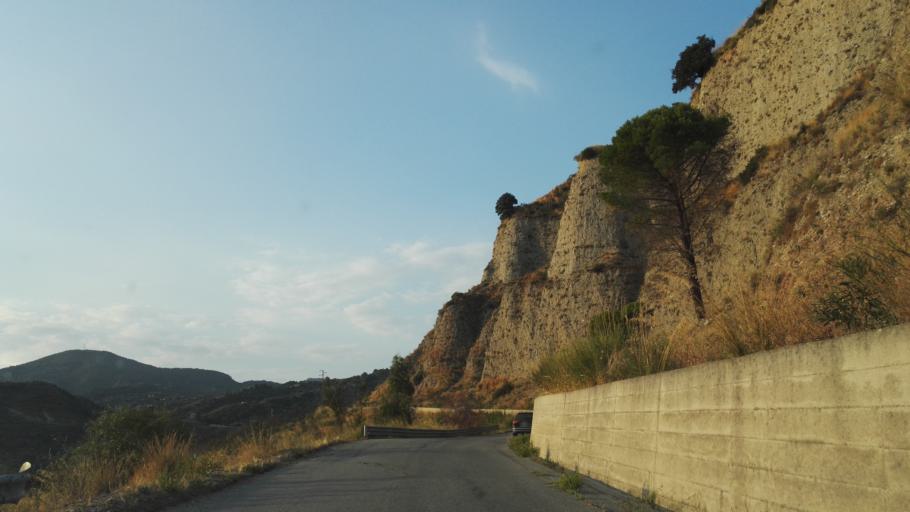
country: IT
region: Calabria
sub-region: Provincia di Reggio Calabria
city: Caulonia
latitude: 38.3990
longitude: 16.4288
